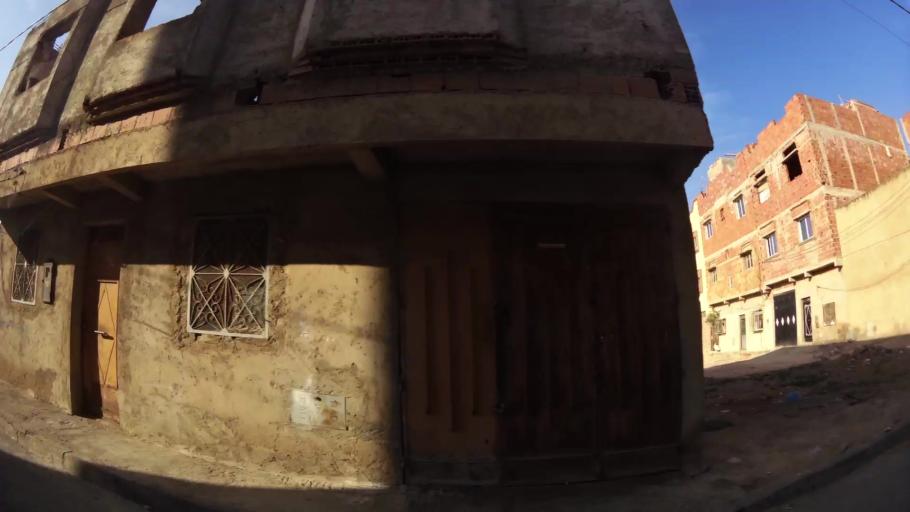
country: MA
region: Oriental
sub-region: Oujda-Angad
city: Oujda
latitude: 34.7119
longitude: -1.9009
